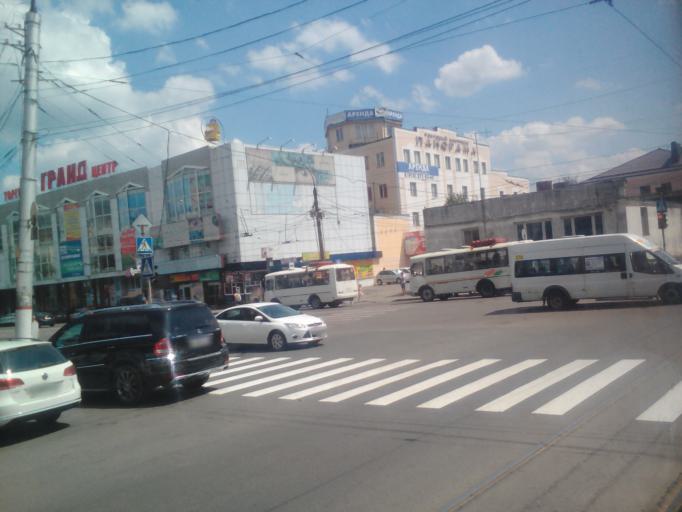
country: RU
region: Kursk
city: Kursk
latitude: 51.7252
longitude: 36.1865
